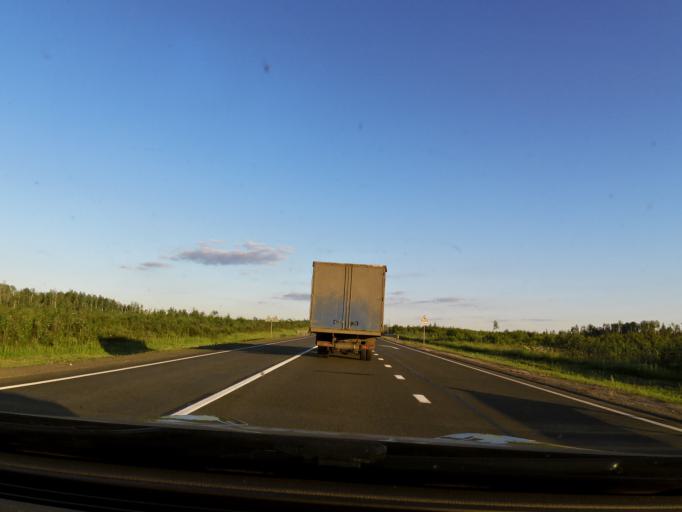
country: RU
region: Jaroslavl
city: Prechistoye
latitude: 58.6303
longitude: 40.3282
